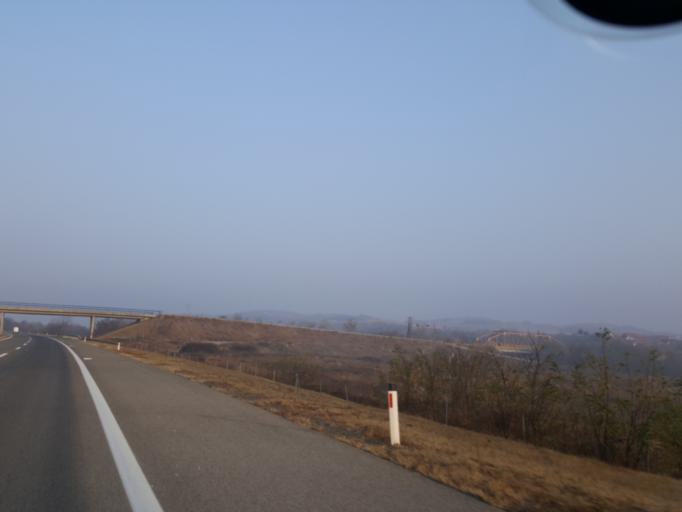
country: RS
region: Central Serbia
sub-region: Jablanicki Okrug
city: Leskovac
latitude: 43.0156
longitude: 22.0215
